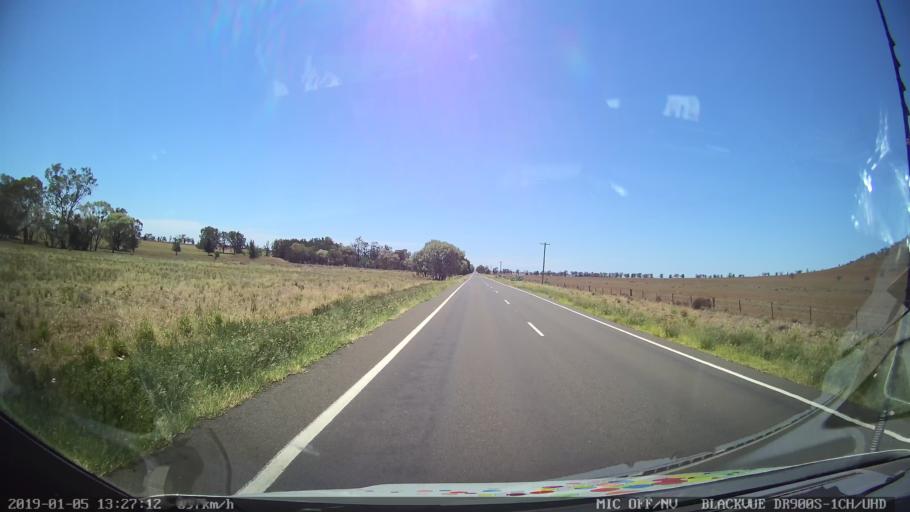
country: AU
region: New South Wales
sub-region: Gunnedah
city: Gunnedah
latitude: -31.0465
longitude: 150.0261
